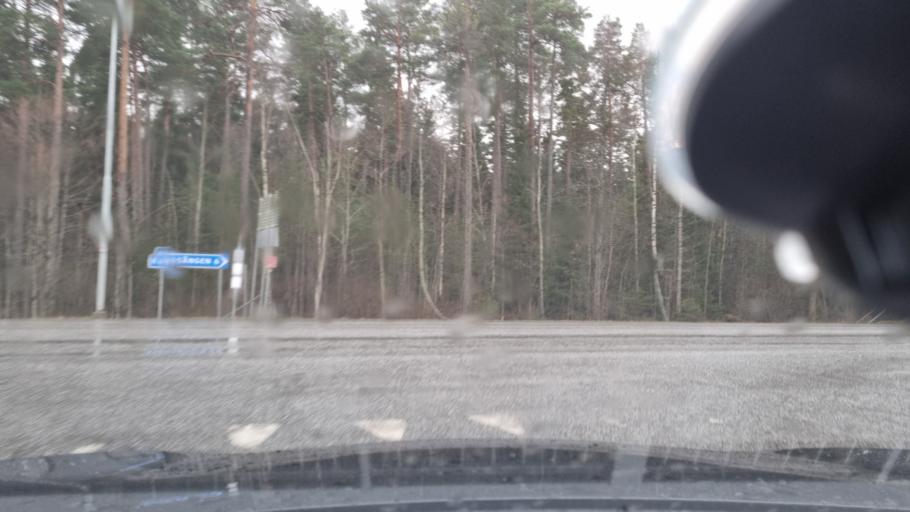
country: SE
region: Stockholm
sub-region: Upplands-Bro Kommun
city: Kungsaengen
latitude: 59.5145
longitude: 17.7600
